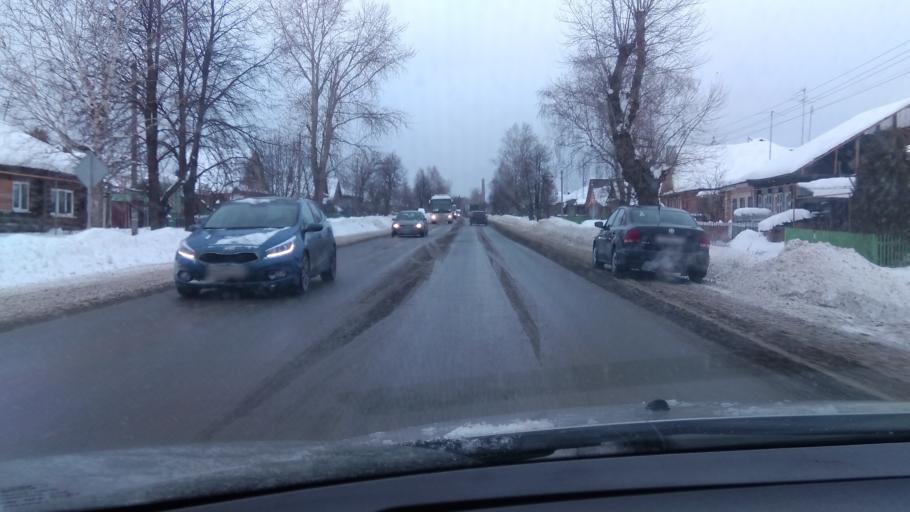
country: RU
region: Sverdlovsk
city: Nikolo-Pavlovskoye
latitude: 57.7891
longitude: 60.0555
